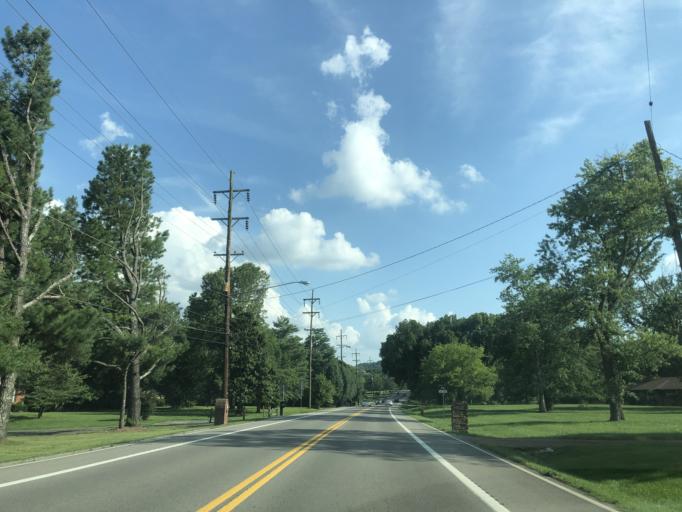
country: US
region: Tennessee
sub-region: Davidson County
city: Nashville
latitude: 36.2401
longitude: -86.8307
